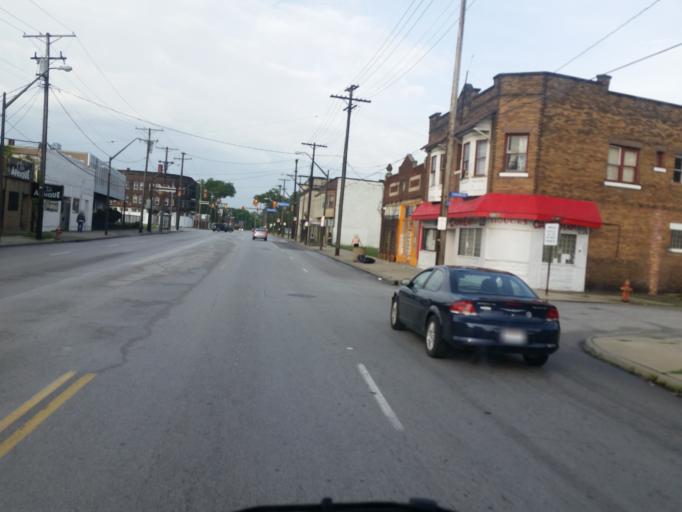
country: US
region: Ohio
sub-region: Cuyahoga County
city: East Cleveland
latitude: 41.5490
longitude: -81.5856
